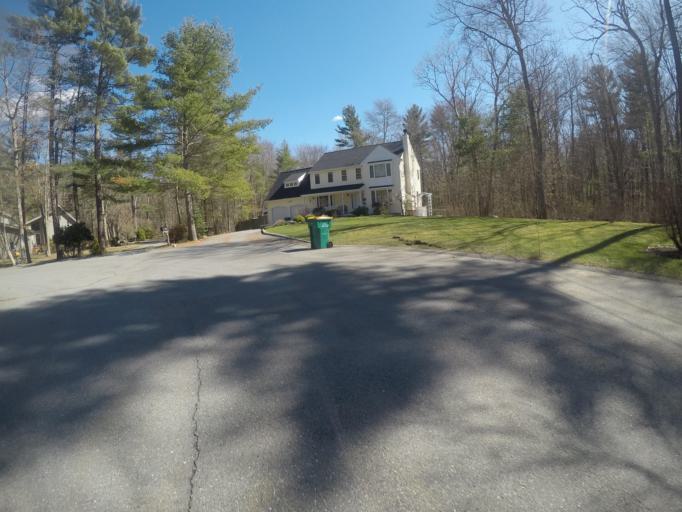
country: US
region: Massachusetts
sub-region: Bristol County
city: Easton
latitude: 42.0056
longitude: -71.1013
